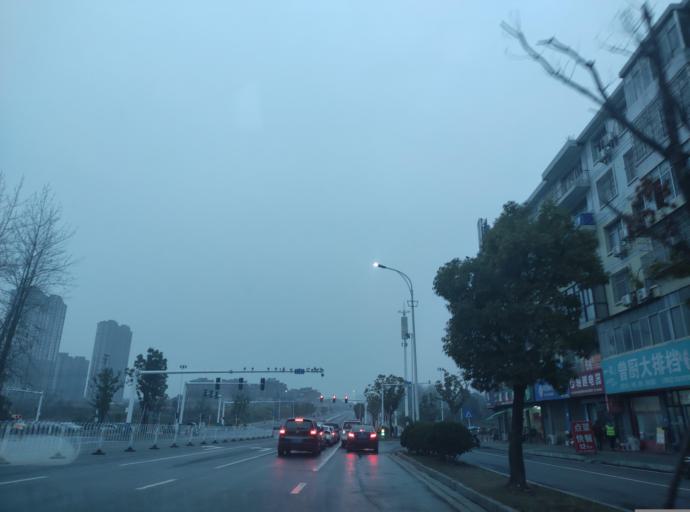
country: CN
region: Jiangxi Sheng
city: Pingxiang
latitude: 27.6687
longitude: 113.8650
